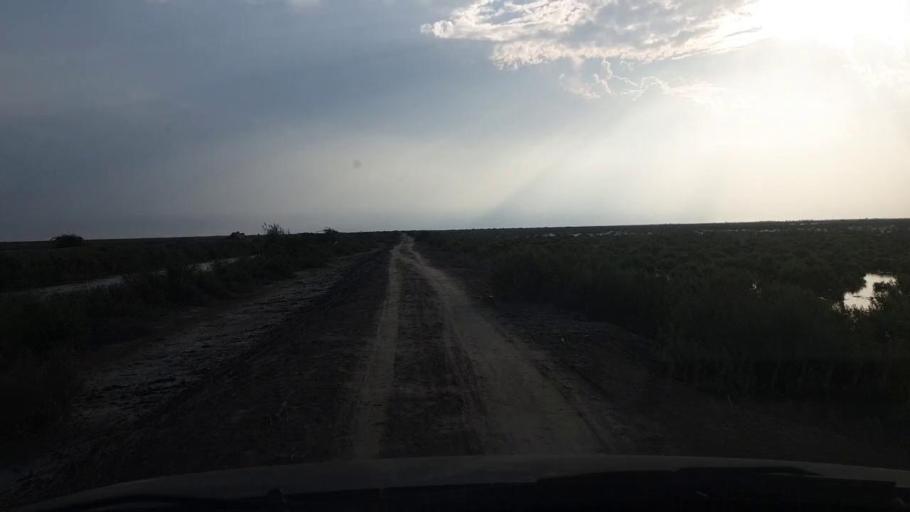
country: PK
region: Sindh
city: Badin
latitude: 24.4368
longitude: 68.6731
